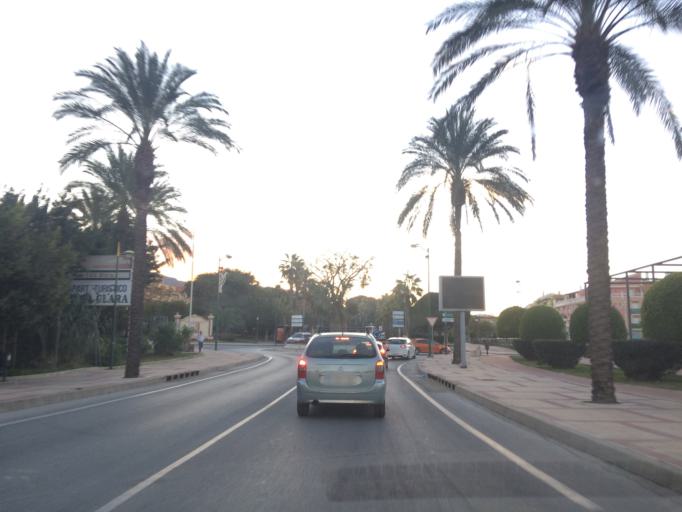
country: ES
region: Andalusia
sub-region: Provincia de Malaga
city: Alhaurin de la Torre
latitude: 36.6606
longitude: -4.5577
